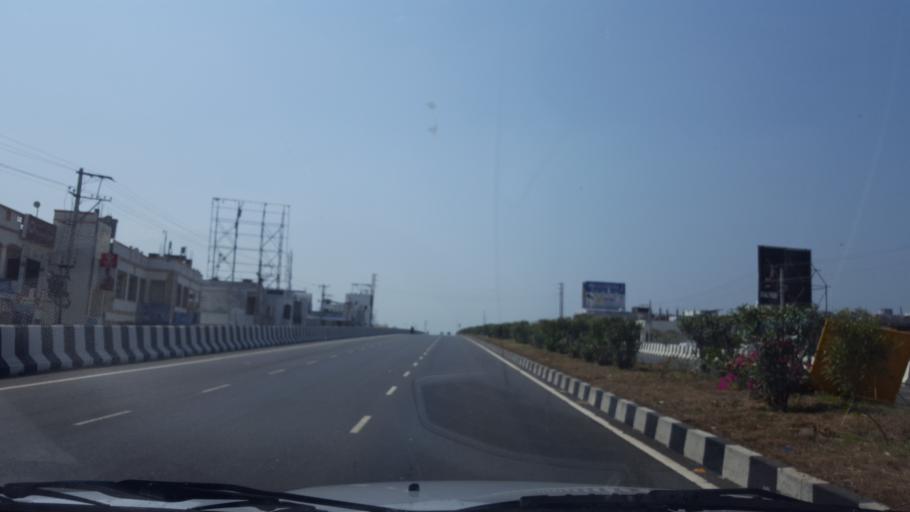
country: IN
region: Andhra Pradesh
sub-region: Guntur
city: Chilakalurupet
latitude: 15.9878
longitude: 80.1049
